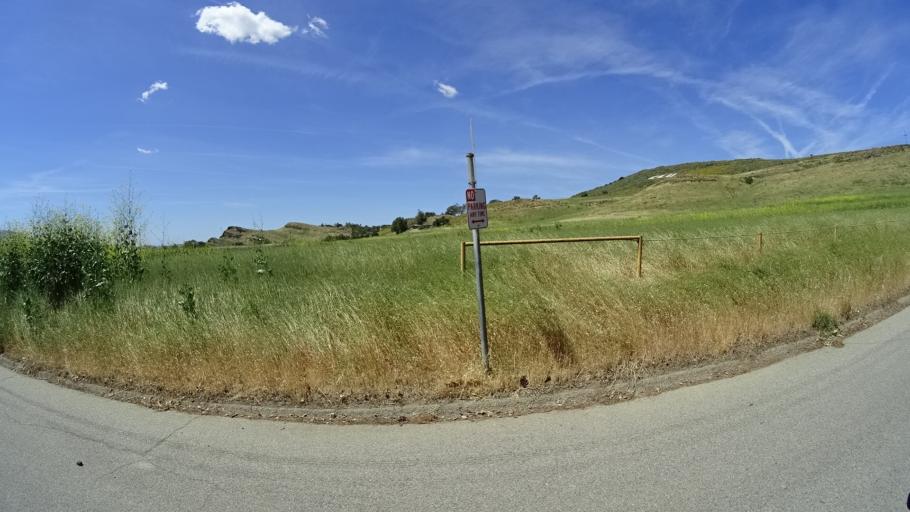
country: US
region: California
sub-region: Ventura County
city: Moorpark
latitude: 34.2315
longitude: -118.8756
